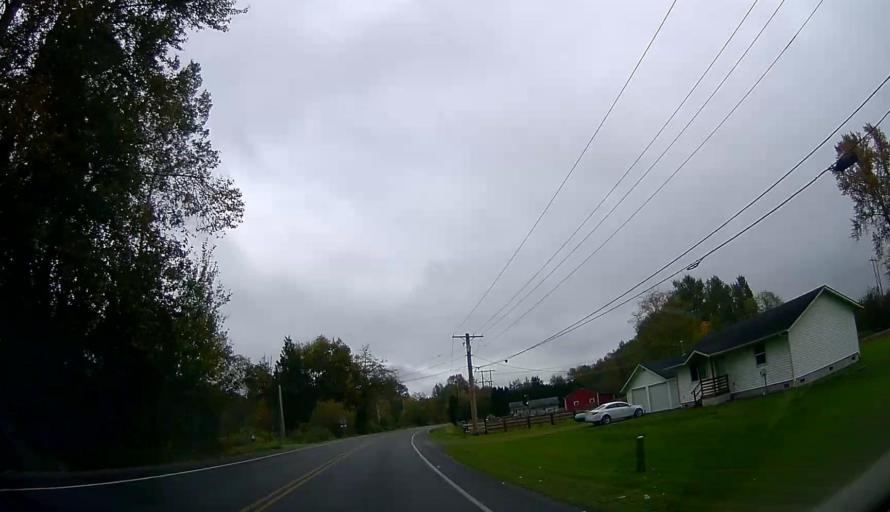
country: US
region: Washington
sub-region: Skagit County
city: Sedro-Woolley
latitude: 48.5235
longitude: -122.1707
